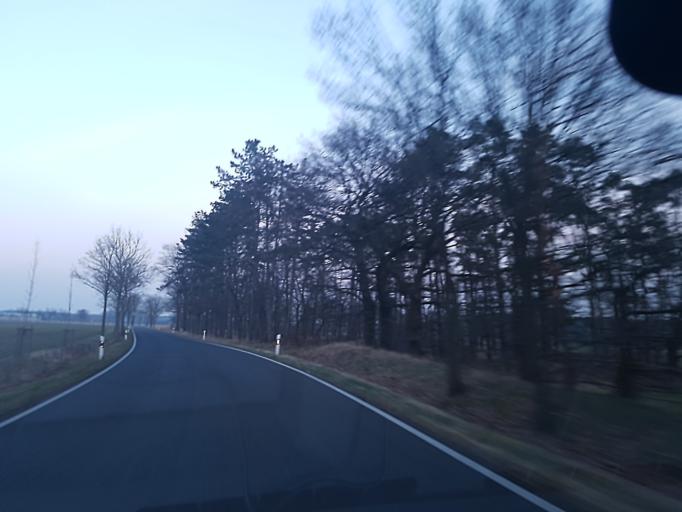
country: DE
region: Brandenburg
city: Herzberg
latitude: 51.7348
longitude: 13.1902
